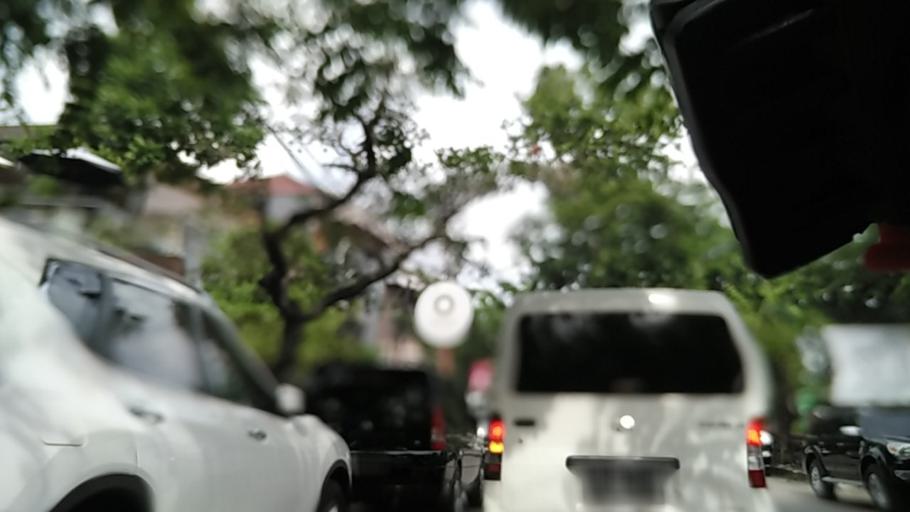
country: ID
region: Central Java
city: Semarang
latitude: -7.0003
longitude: 110.4263
